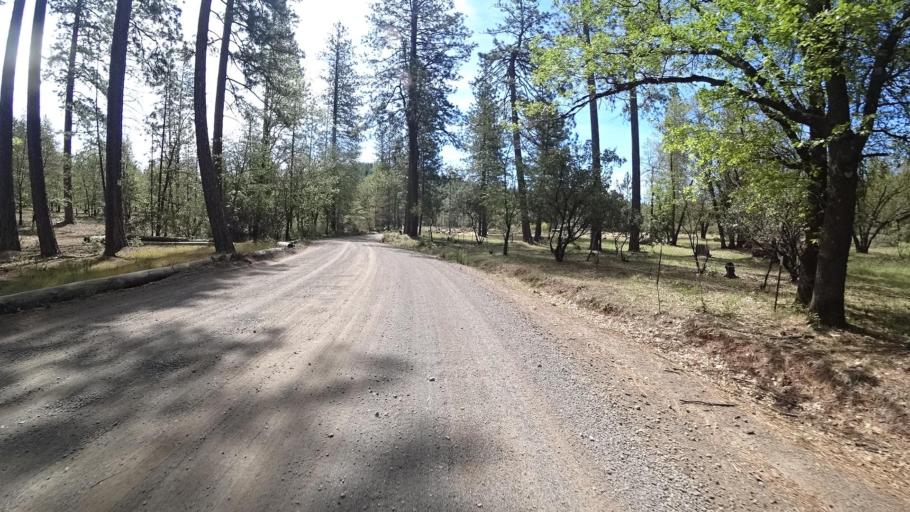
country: US
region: California
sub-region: Lake County
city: Cobb
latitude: 38.8685
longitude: -122.7451
